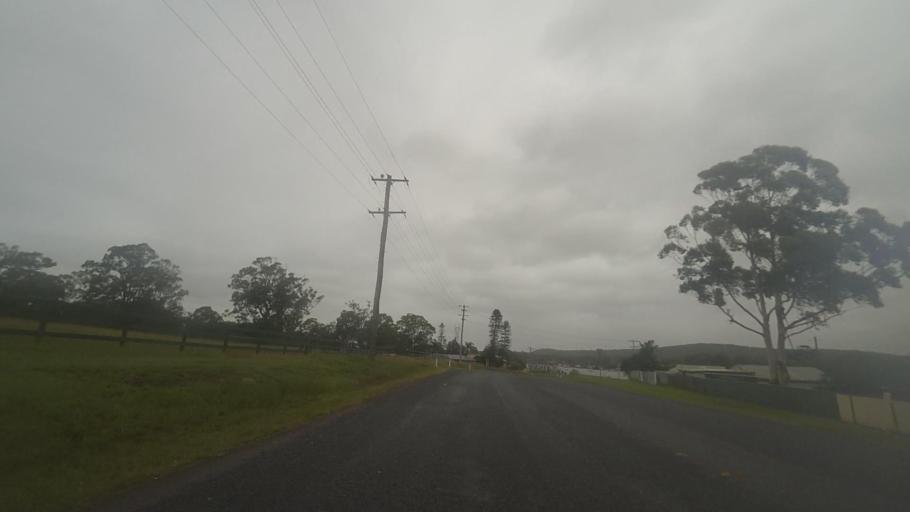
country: AU
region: New South Wales
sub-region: Port Stephens Shire
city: Port Stephens
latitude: -32.6523
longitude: 151.9718
